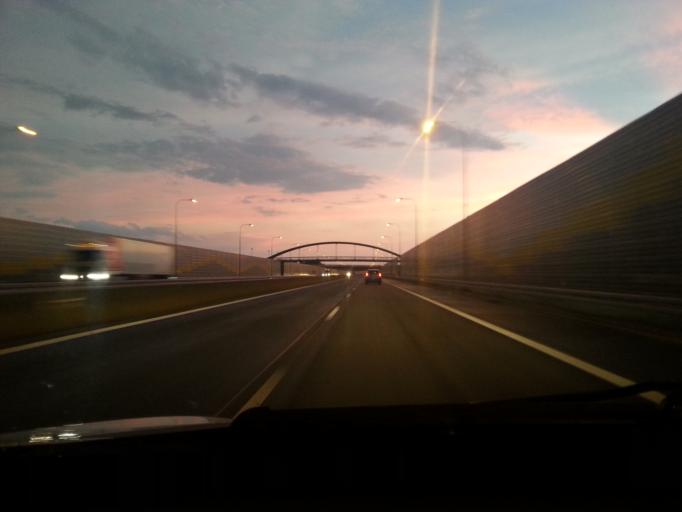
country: PL
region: Lodz Voivodeship
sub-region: Powiat zdunskowolski
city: Zdunska Wola
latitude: 51.5753
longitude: 18.9393
